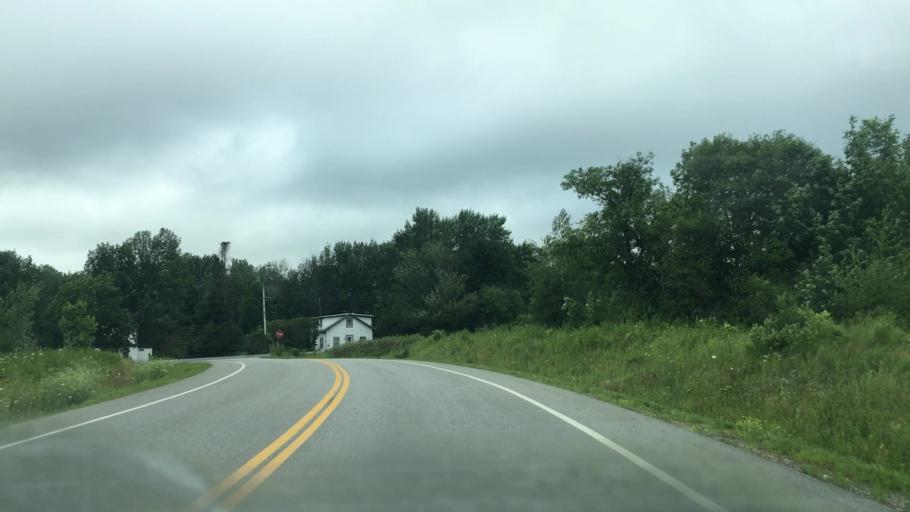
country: US
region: Maine
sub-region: Penobscot County
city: Veazie
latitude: 44.8429
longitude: -68.7444
